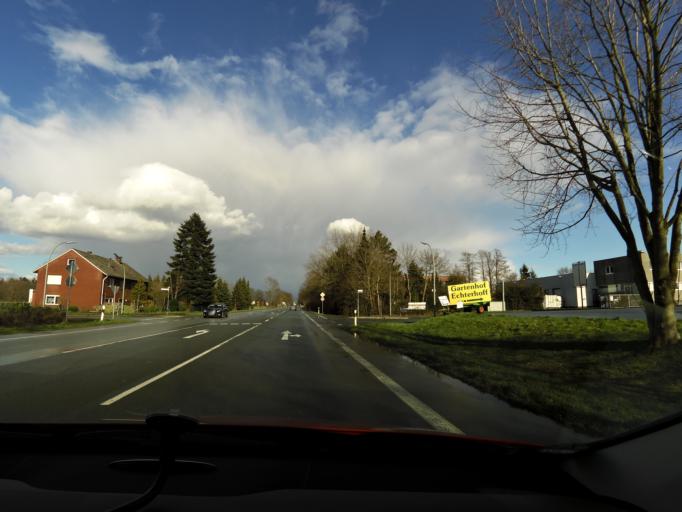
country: DE
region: North Rhine-Westphalia
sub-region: Regierungsbezirk Detmold
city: Verl
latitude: 51.8766
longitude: 8.4650
